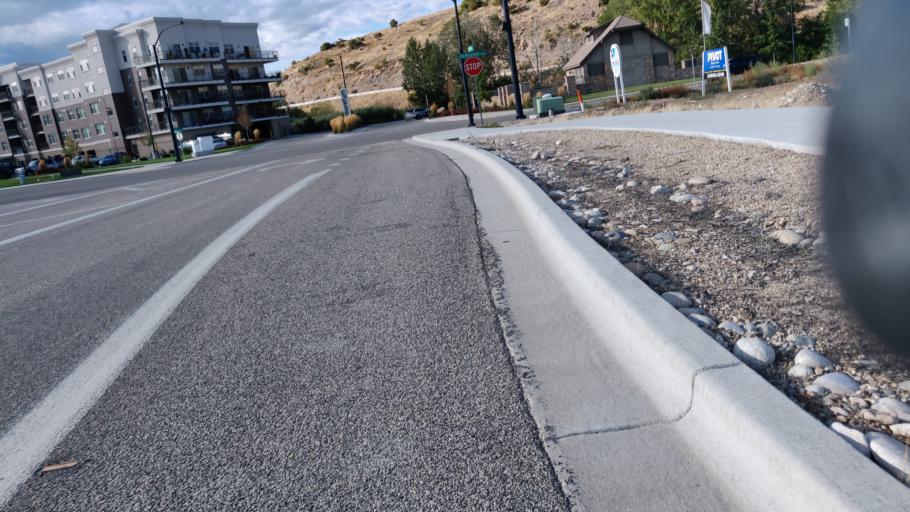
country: US
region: Idaho
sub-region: Ada County
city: Boise
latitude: 43.5769
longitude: -116.1485
